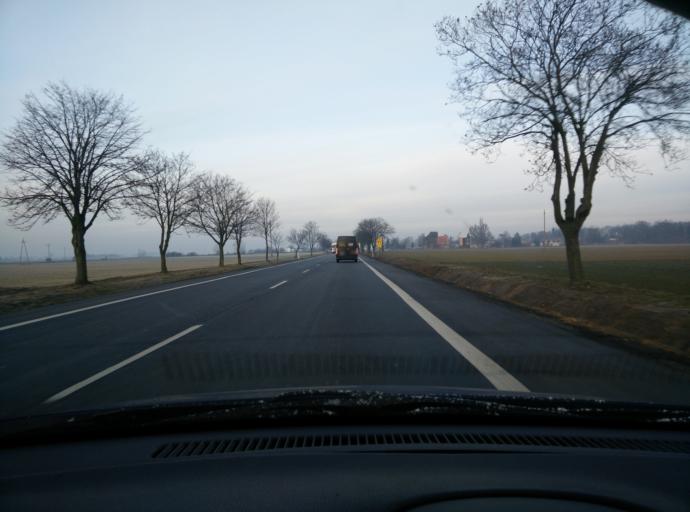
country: PL
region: Greater Poland Voivodeship
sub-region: Powiat sredzki
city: Sroda Wielkopolska
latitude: 52.2297
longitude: 17.2065
